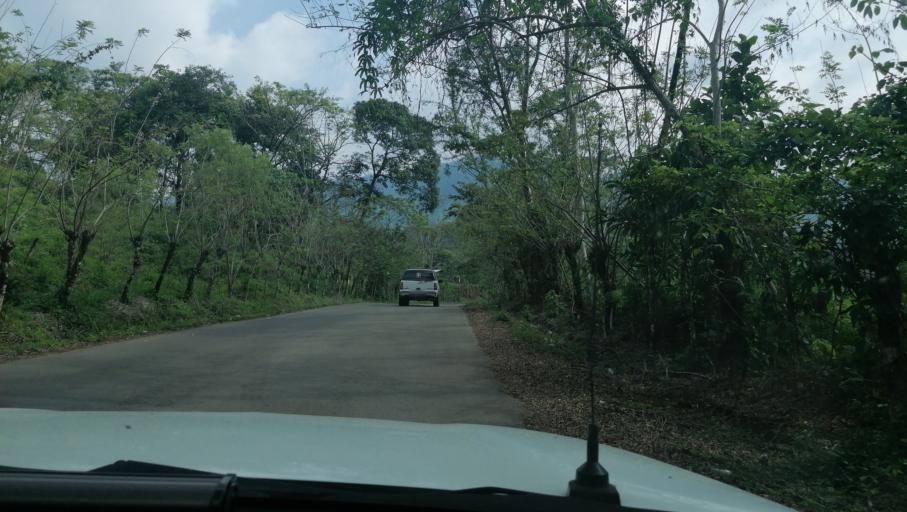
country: MX
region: Chiapas
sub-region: Francisco Leon
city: San Miguel la Sardina
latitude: 17.2252
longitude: -93.3434
